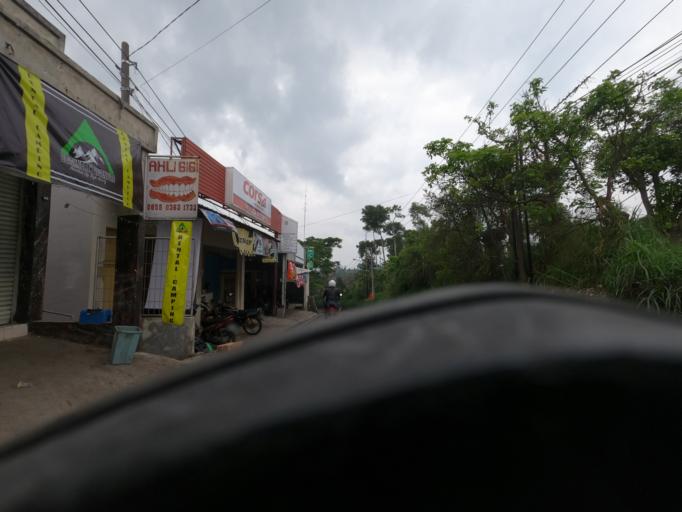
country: ID
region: West Java
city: Lembang
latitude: -6.8087
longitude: 107.5694
